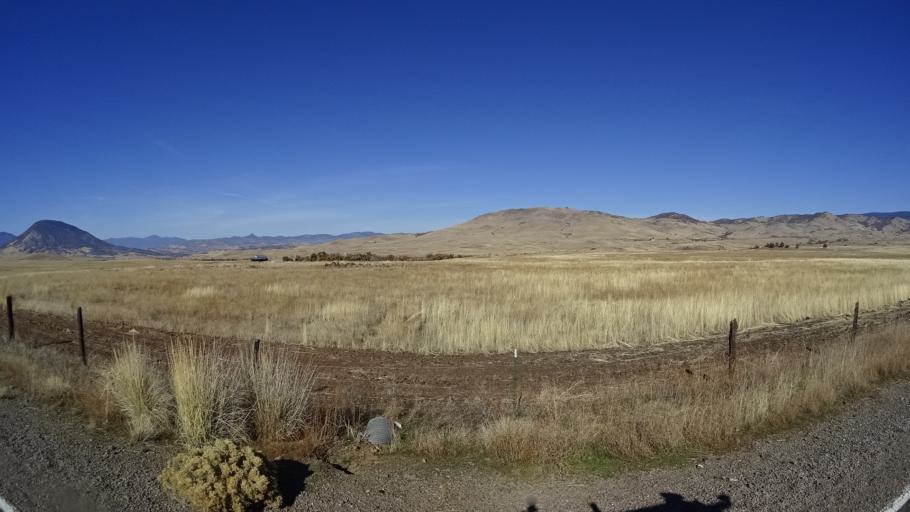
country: US
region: California
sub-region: Siskiyou County
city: Montague
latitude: 41.8044
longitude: -122.4113
